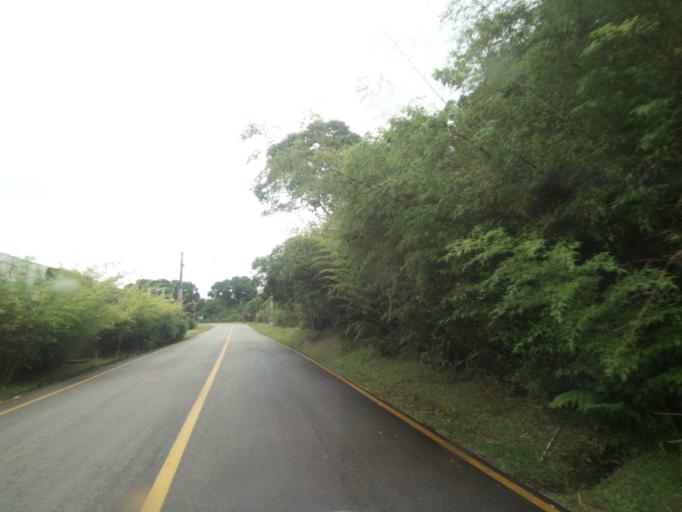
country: BR
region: Parana
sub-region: Curitiba
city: Curitiba
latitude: -25.4273
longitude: -49.3134
